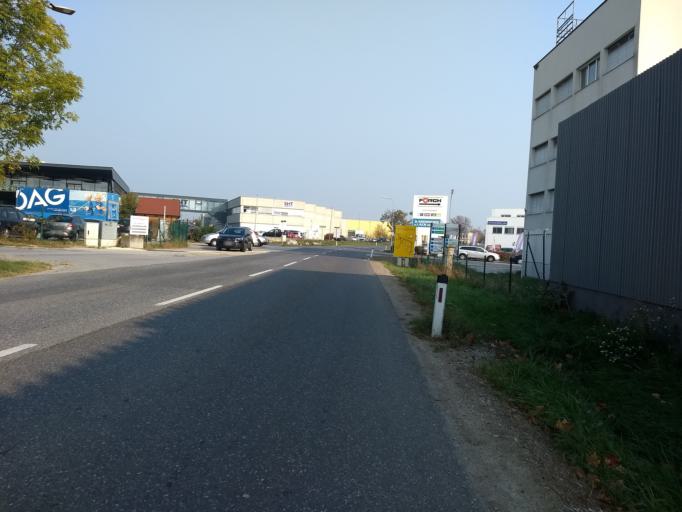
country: AT
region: Lower Austria
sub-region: Politischer Bezirk Modling
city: Brunn am Gebirge
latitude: 48.1191
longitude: 16.2901
